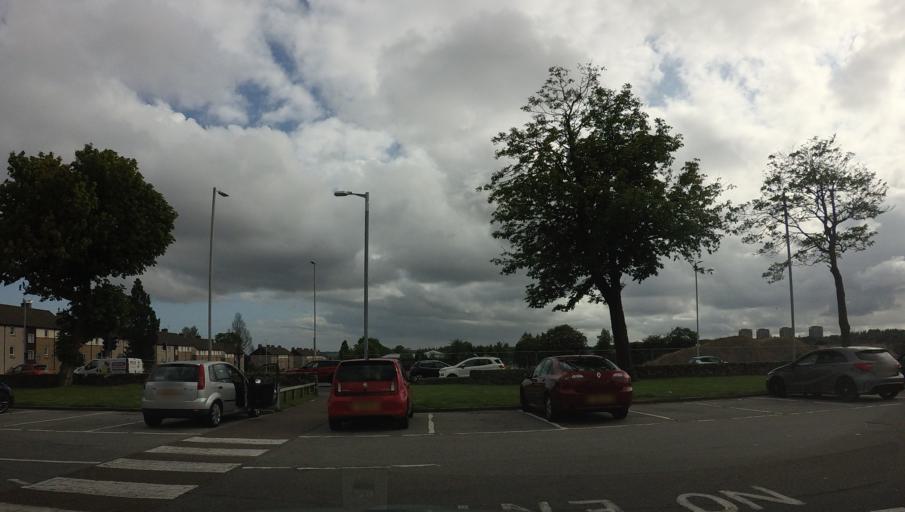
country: GB
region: Scotland
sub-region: Aberdeen City
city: Cults
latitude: 57.1515
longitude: -2.1622
